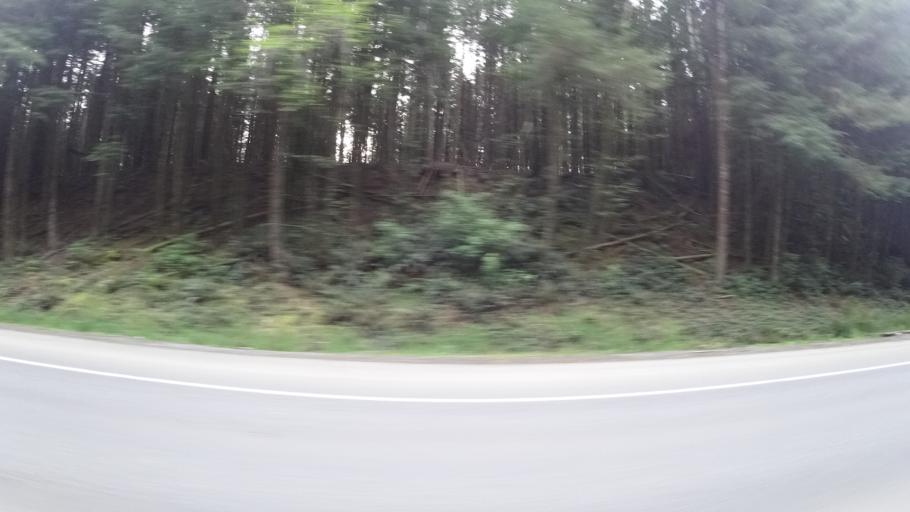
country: US
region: Oregon
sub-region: Coos County
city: Barview
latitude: 43.2418
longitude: -124.2883
